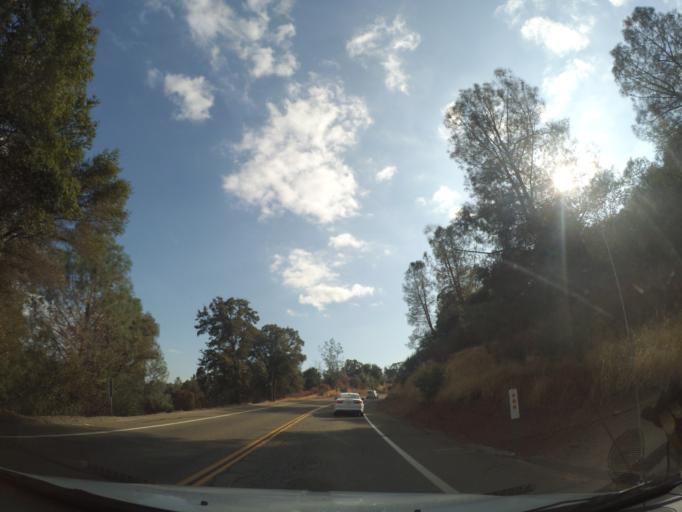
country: US
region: California
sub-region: Mariposa County
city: Mariposa
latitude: 37.5100
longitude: -119.9641
